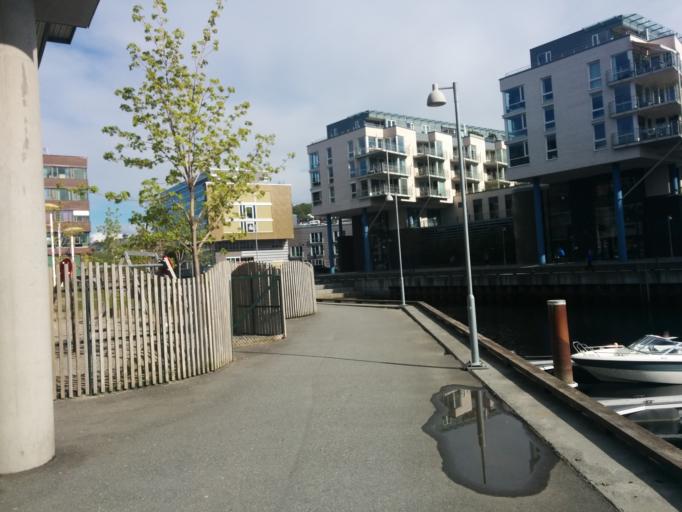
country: NO
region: Sor-Trondelag
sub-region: Trondheim
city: Trondheim
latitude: 63.4361
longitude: 10.4131
